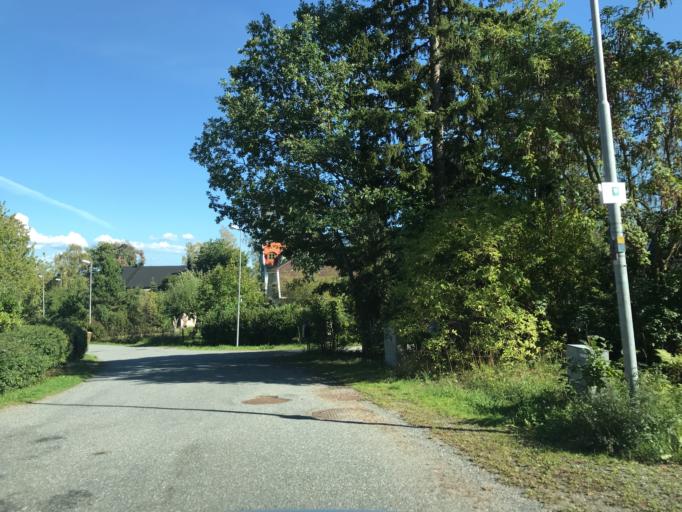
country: SE
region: Stockholm
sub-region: Sollentuna Kommun
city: Sollentuna
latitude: 59.4296
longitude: 17.9289
